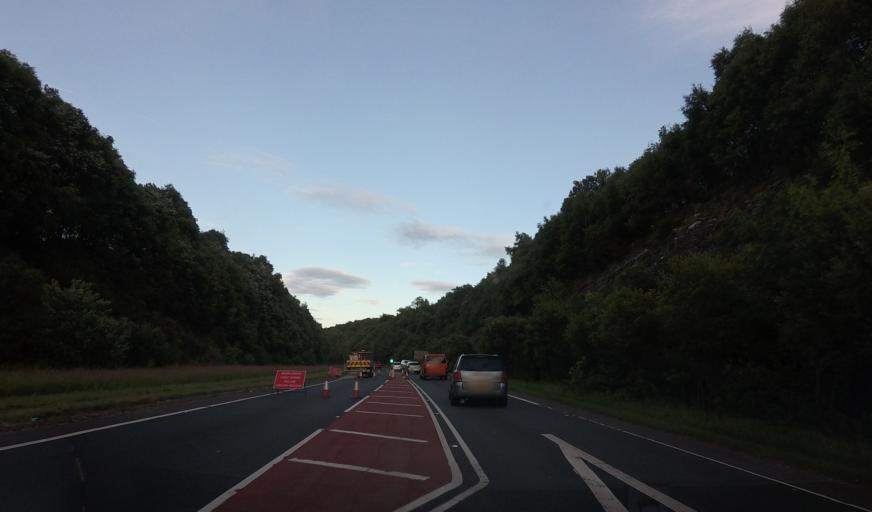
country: GB
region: Scotland
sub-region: Argyll and Bute
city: Helensburgh
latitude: 56.1691
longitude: -4.6767
